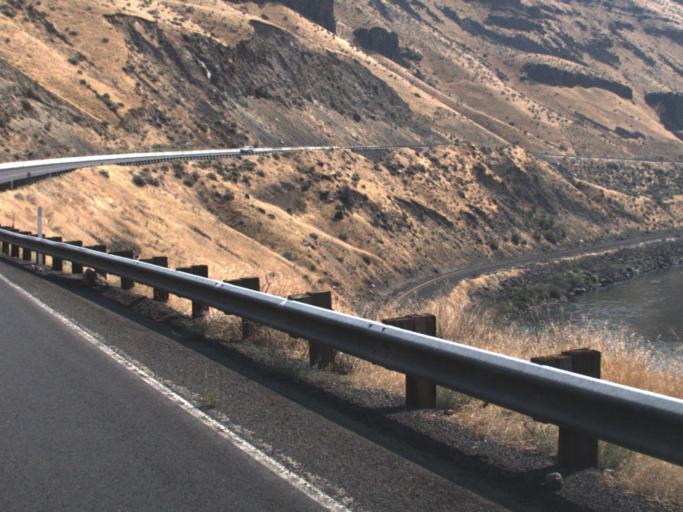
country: US
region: Washington
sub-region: Yakima County
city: Selah
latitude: 46.7277
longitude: -120.4509
